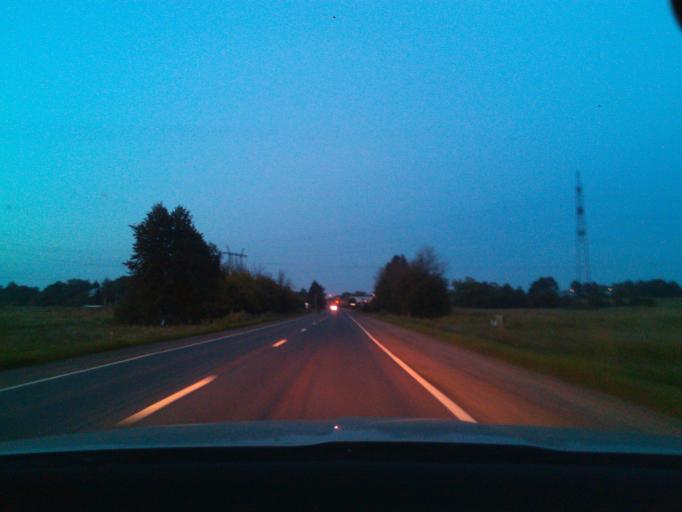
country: RU
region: Moskovskaya
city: Solnechnogorsk
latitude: 56.1459
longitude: 36.9088
